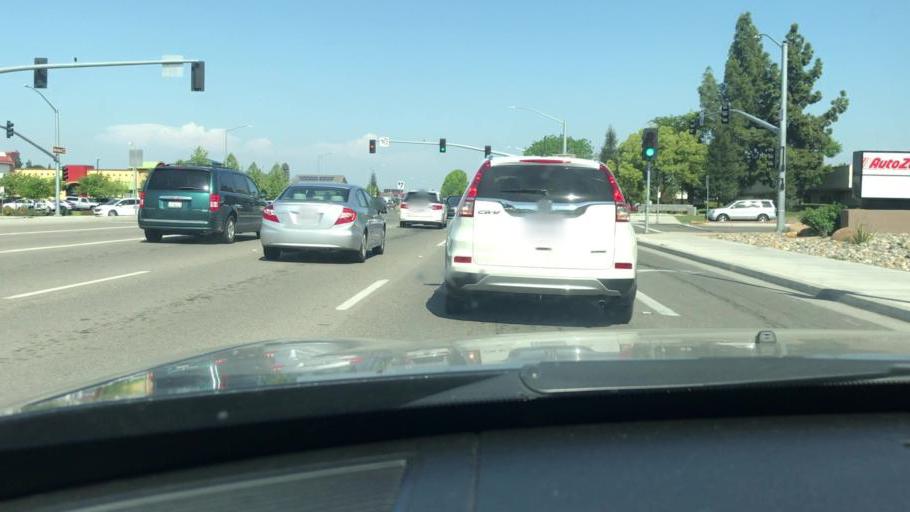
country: US
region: California
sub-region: Fresno County
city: Clovis
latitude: 36.8374
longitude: -119.6916
